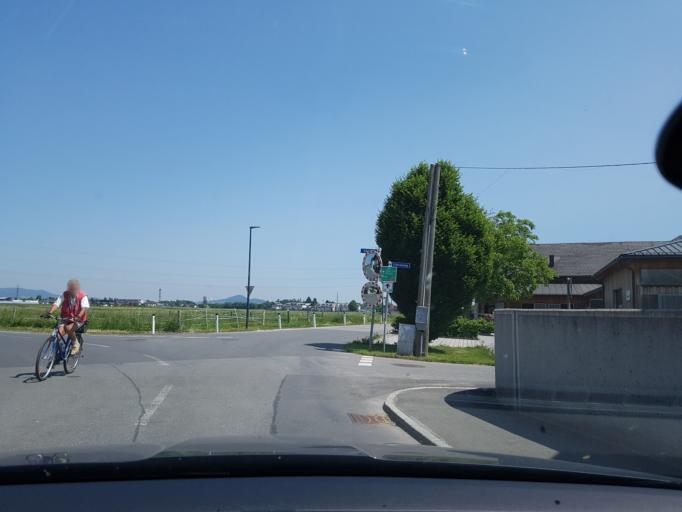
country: DE
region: Bavaria
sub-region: Upper Bavaria
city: Ainring
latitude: 47.7764
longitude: 12.9735
